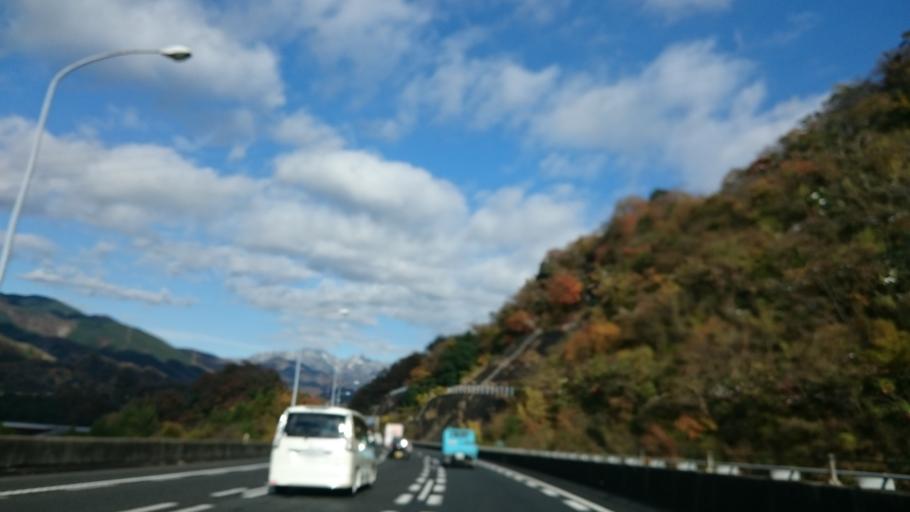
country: JP
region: Shizuoka
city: Gotemba
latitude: 35.3514
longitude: 139.0105
